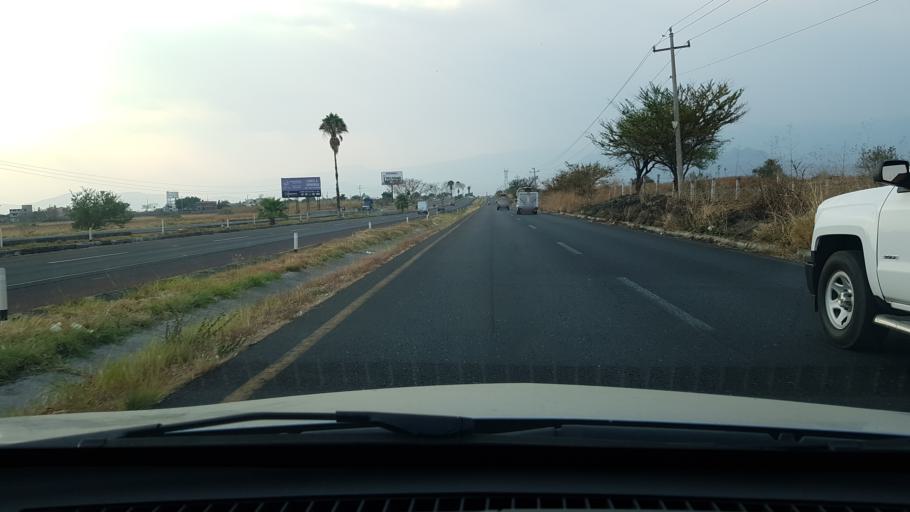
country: MX
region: Morelos
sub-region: Cuautla
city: Tierra Larga (Campo Nuevo)
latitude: 18.8708
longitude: -98.9548
